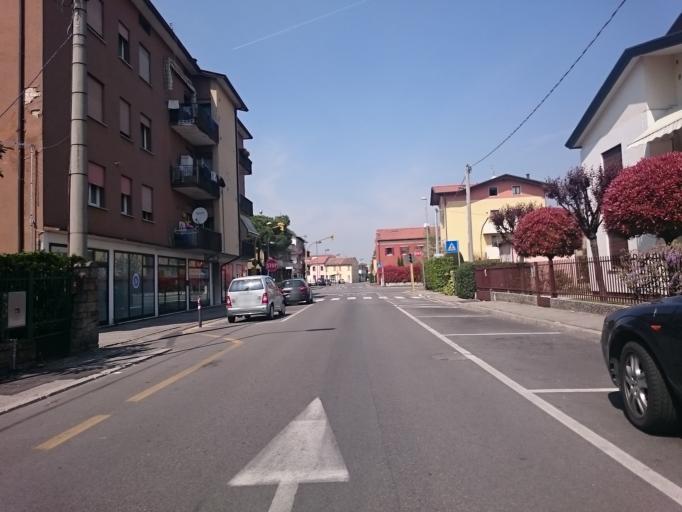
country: IT
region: Veneto
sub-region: Provincia di Padova
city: Tencarola
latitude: 45.3919
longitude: 11.8085
